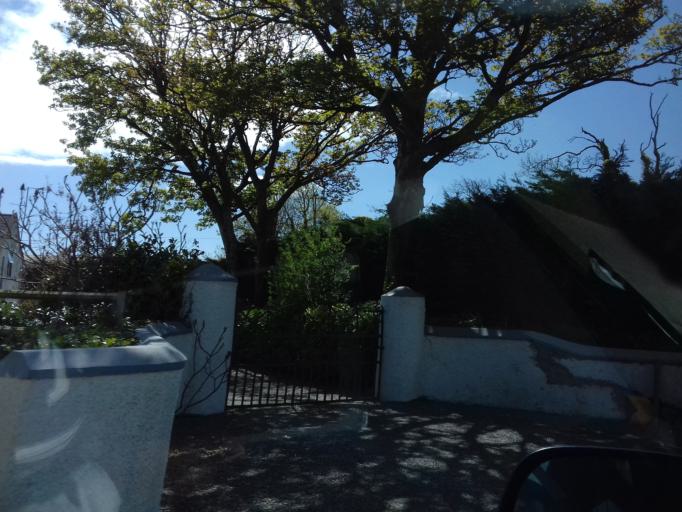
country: IE
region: Munster
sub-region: Waterford
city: Dunmore East
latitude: 52.2385
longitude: -6.8545
